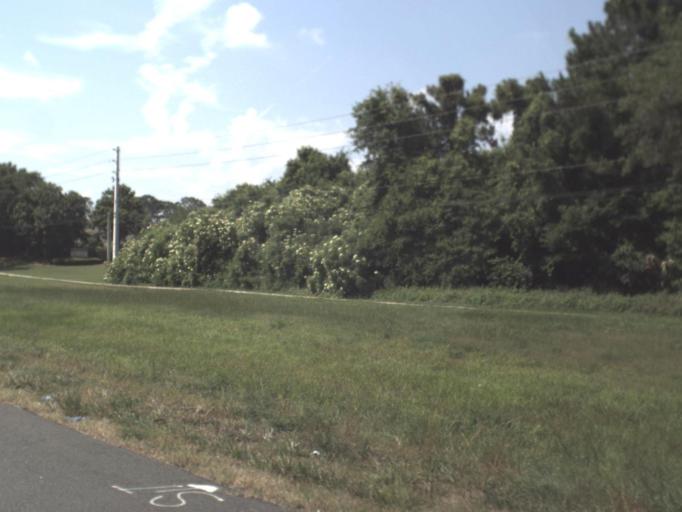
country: US
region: Florida
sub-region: Saint Johns County
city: Palm Valley
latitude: 30.1769
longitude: -81.3763
